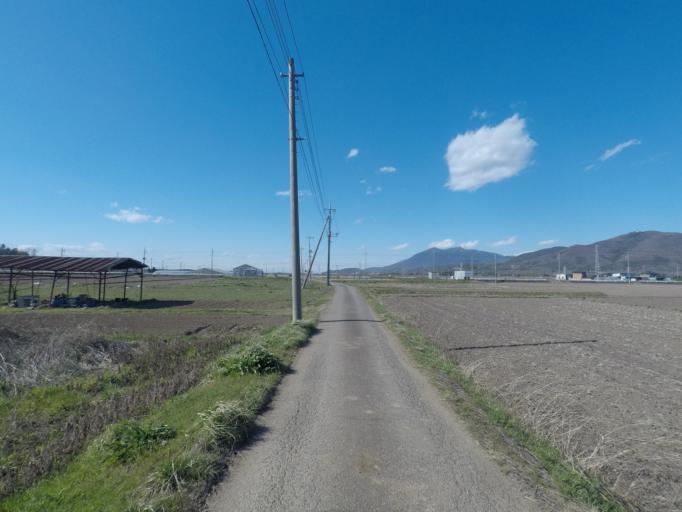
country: JP
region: Ibaraki
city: Tsukuba
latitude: 36.1296
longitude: 140.1149
